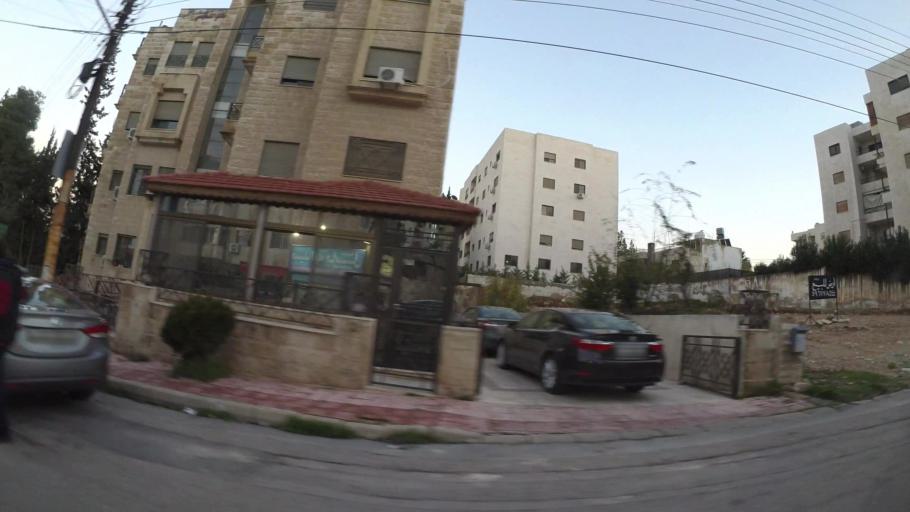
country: JO
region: Amman
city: Al Jubayhah
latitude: 31.9927
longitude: 35.8858
